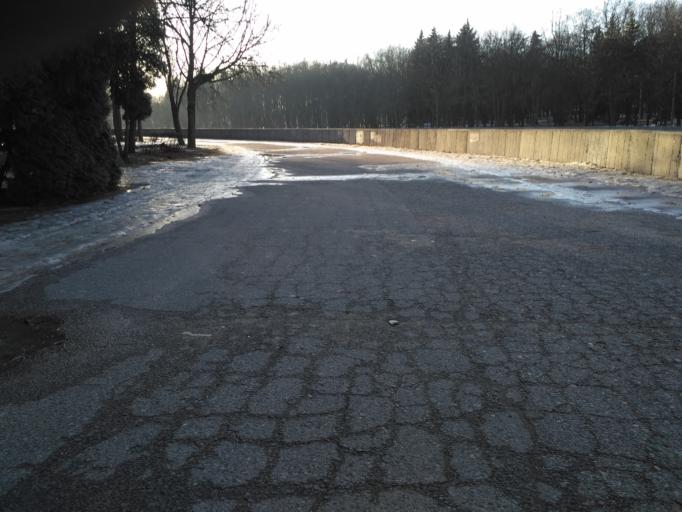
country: BY
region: Minsk
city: Minsk
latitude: 53.9085
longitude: 27.5675
